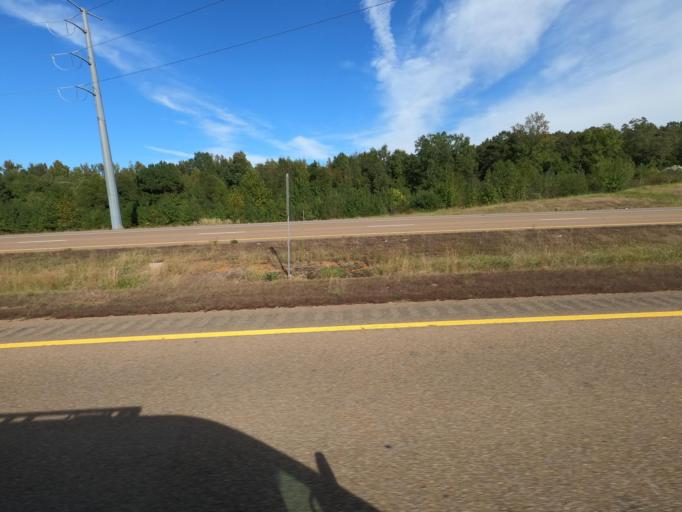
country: US
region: Tennessee
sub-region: Fayette County
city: Piperton
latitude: 35.0667
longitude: -89.6396
